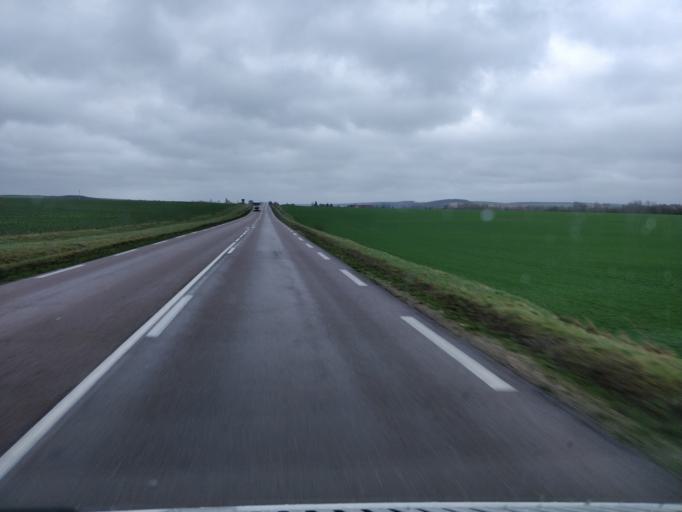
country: FR
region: Champagne-Ardenne
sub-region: Departement de l'Aube
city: Aix-en-Othe
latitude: 48.2359
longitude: 3.5763
